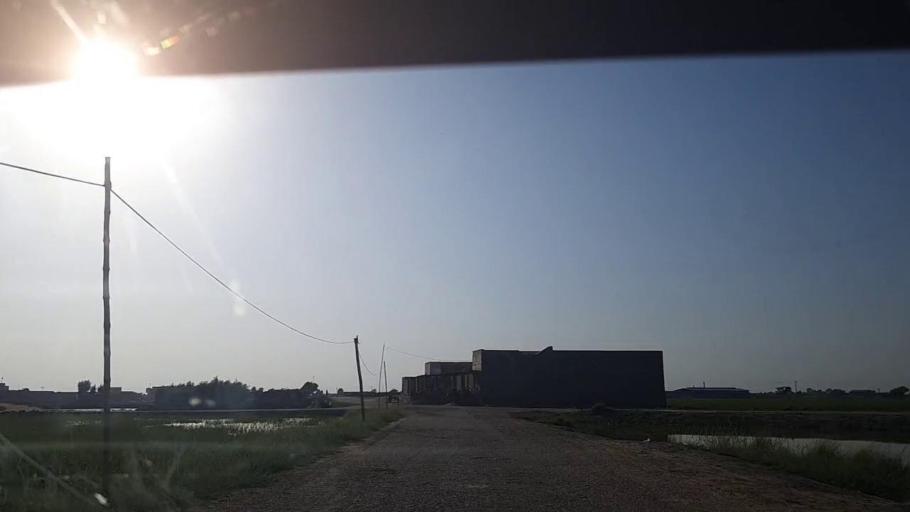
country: PK
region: Sindh
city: Tangwani
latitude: 28.2611
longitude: 69.0080
